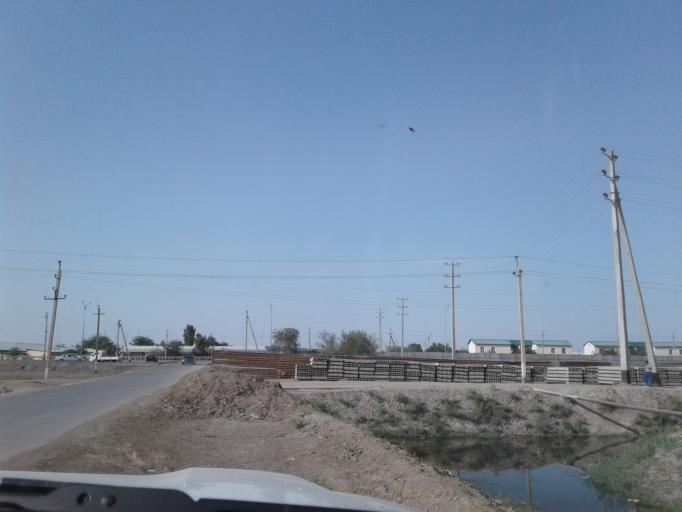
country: TM
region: Dasoguz
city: Dasoguz
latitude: 41.8498
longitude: 59.9235
